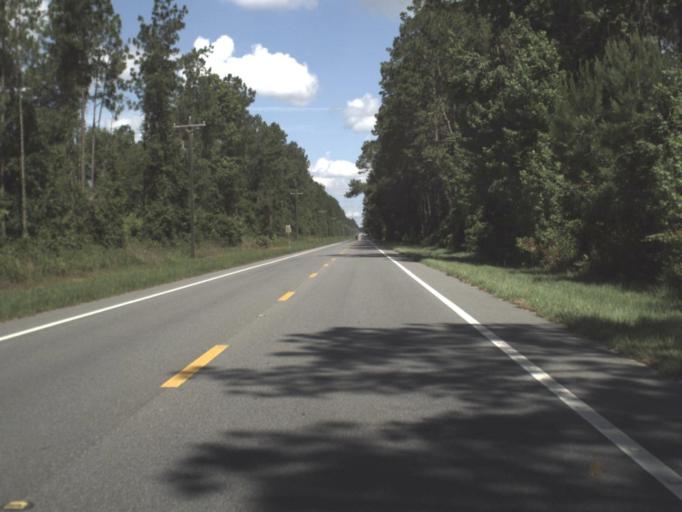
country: US
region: Florida
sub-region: Putnam County
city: Palatka
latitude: 29.6994
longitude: -81.7666
